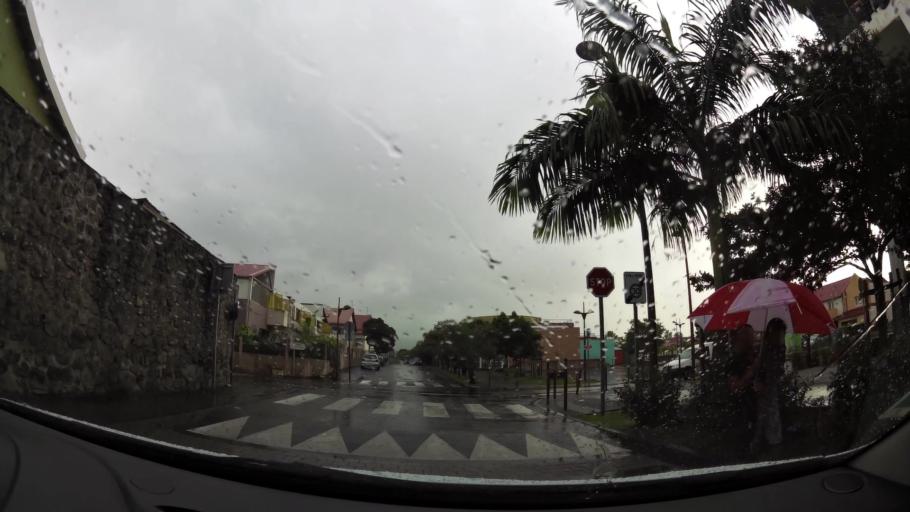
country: RE
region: Reunion
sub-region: Reunion
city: Saint-Andre
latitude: -20.9761
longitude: 55.6579
